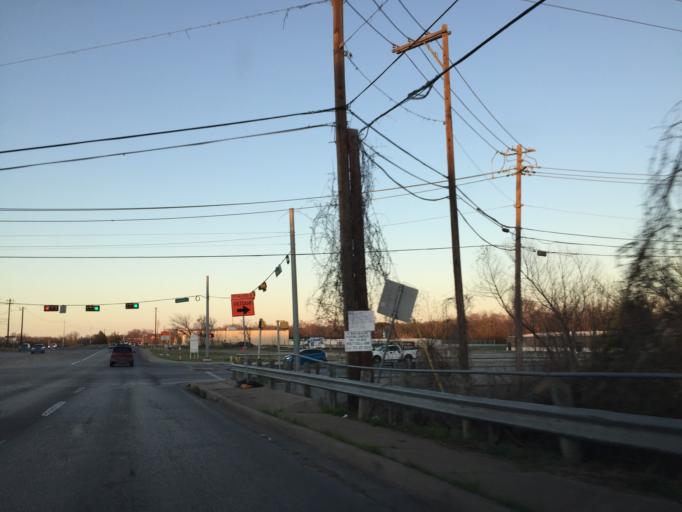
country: US
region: Texas
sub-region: Travis County
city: Pflugerville
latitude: 30.4030
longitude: -97.6387
